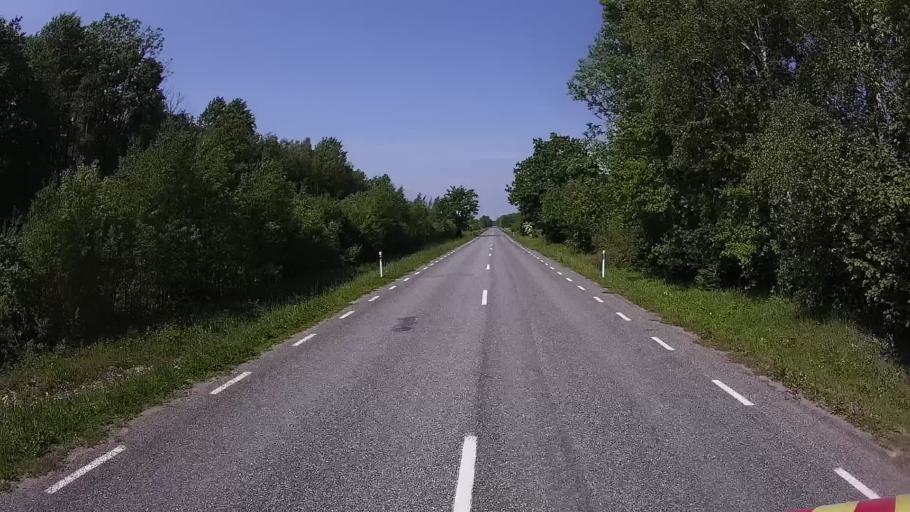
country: EE
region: Saare
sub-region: Kuressaare linn
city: Kuressaare
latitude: 58.3666
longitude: 22.0523
